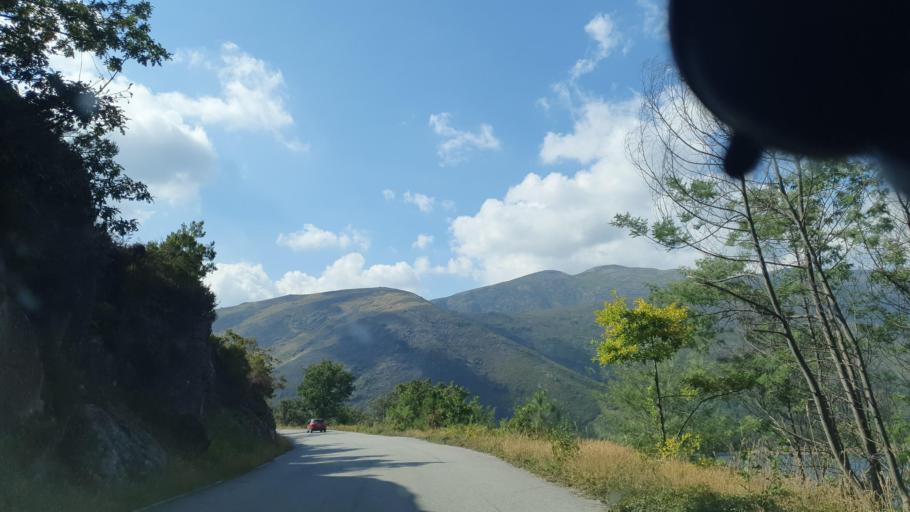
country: PT
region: Braga
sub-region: Terras de Bouro
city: Antas
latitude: 41.7681
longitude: -8.1923
